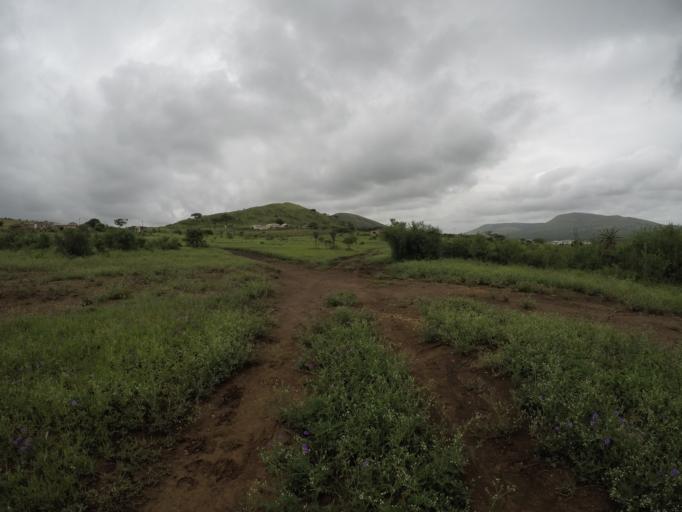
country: ZA
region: KwaZulu-Natal
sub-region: uThungulu District Municipality
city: Empangeni
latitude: -28.6016
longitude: 31.8628
